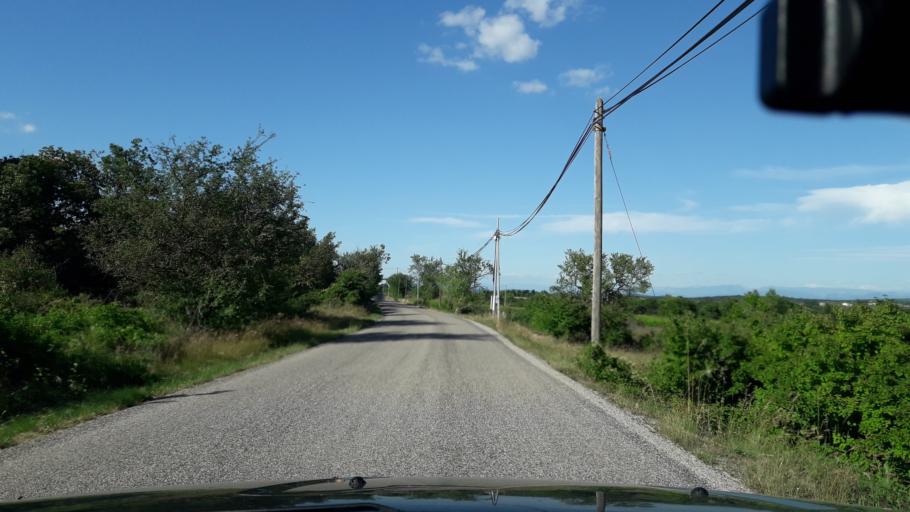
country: FR
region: Languedoc-Roussillon
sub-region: Departement du Gard
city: Saint-Julien-de-Peyrolas
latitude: 44.3842
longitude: 4.5084
